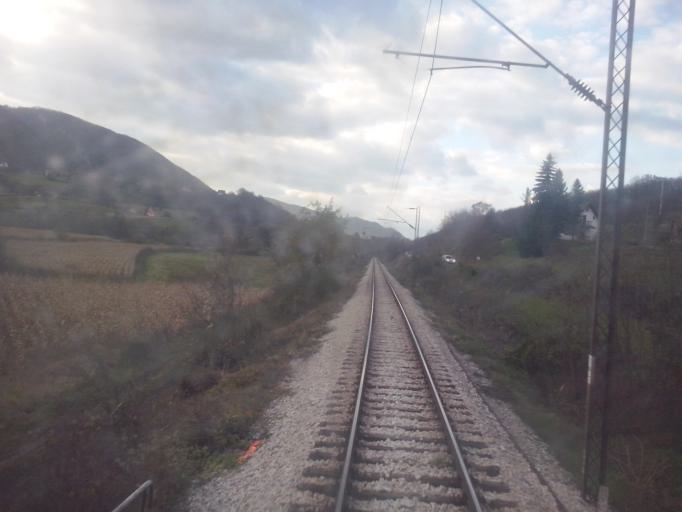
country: RS
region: Central Serbia
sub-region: Zlatiborski Okrug
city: Kosjeric
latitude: 43.9771
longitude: 19.9507
